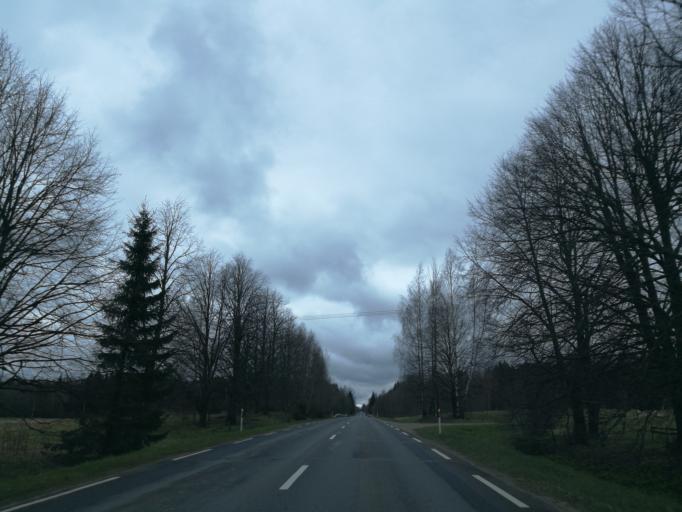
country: LT
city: Rietavas
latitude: 55.7001
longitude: 21.7001
